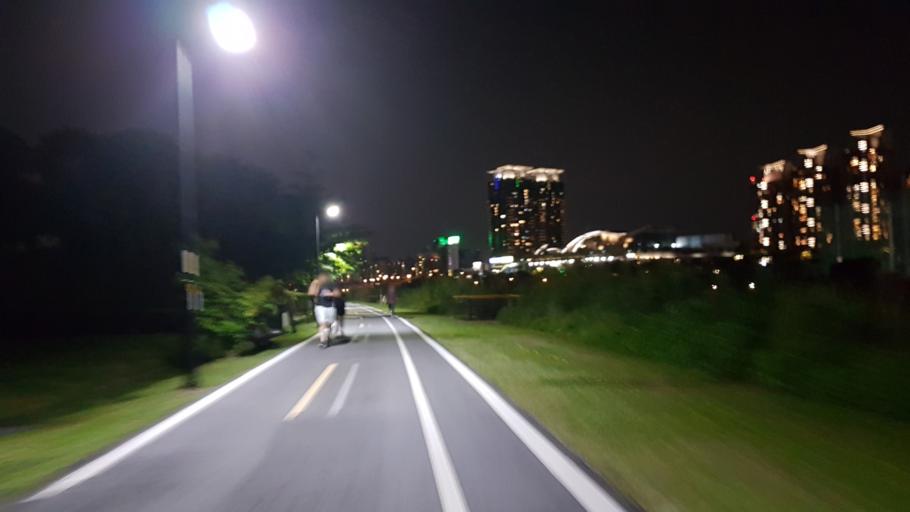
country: TW
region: Taipei
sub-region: Taipei
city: Banqiao
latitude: 24.9654
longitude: 121.5326
